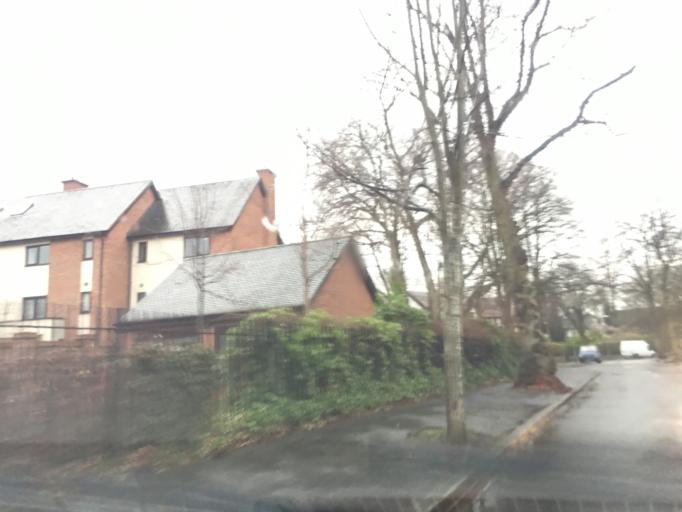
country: GB
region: England
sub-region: Manchester
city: Chorlton cum Hardy
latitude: 53.4248
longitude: -2.2603
